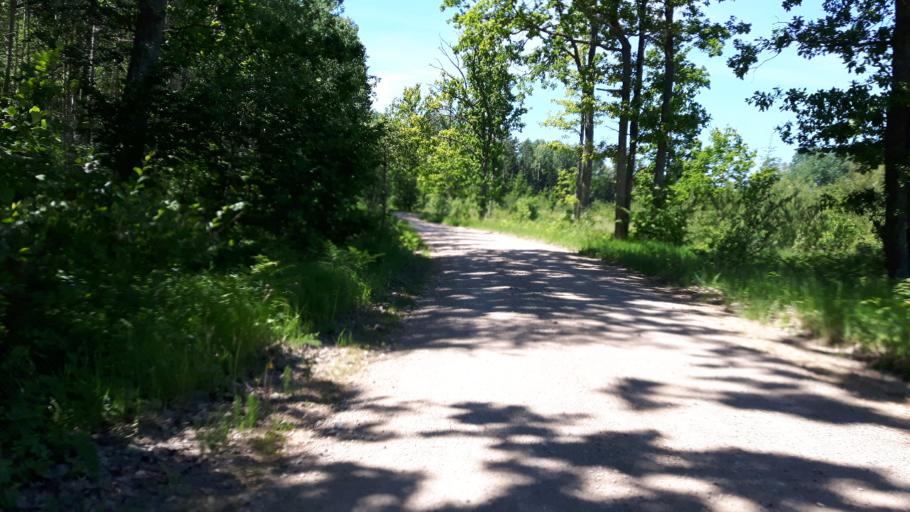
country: LV
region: Kandava
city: Kandava
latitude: 57.0430
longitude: 22.8507
